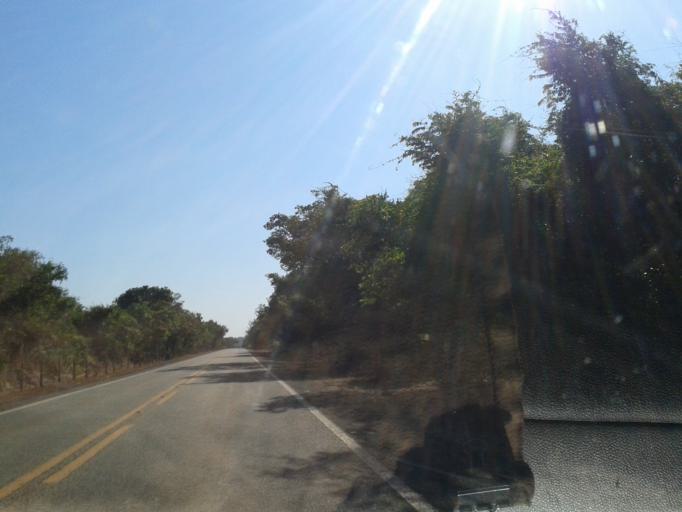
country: BR
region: Goias
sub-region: Mozarlandia
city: Mozarlandia
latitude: -14.6691
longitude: -50.5336
